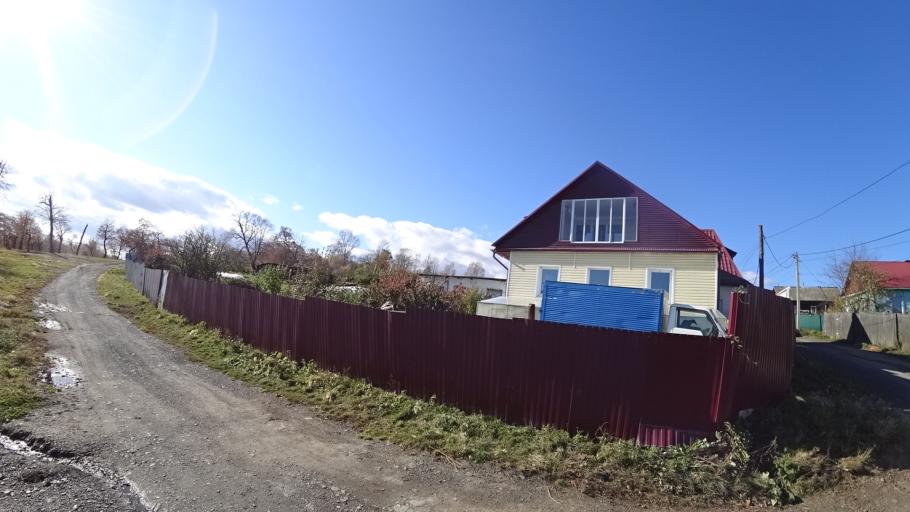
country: RU
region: Khabarovsk Krai
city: Amursk
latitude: 50.2310
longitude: 136.9180
